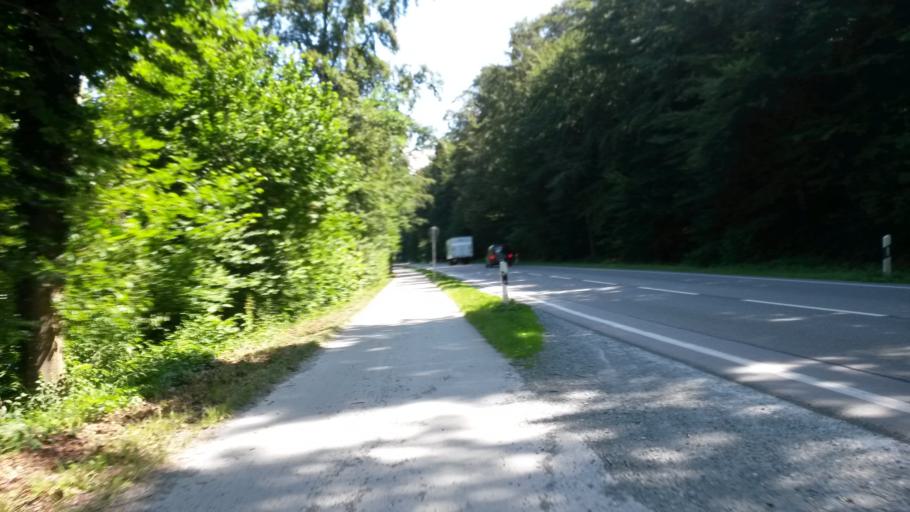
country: DE
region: Bavaria
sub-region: Upper Bavaria
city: Chieming
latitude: 47.8766
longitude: 12.5295
